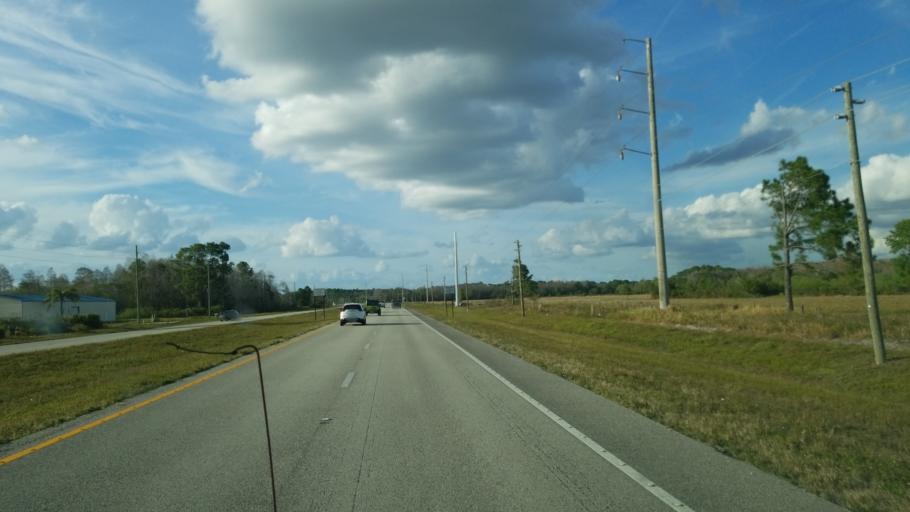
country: US
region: Florida
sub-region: Osceola County
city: Saint Cloud
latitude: 28.1750
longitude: -81.1317
